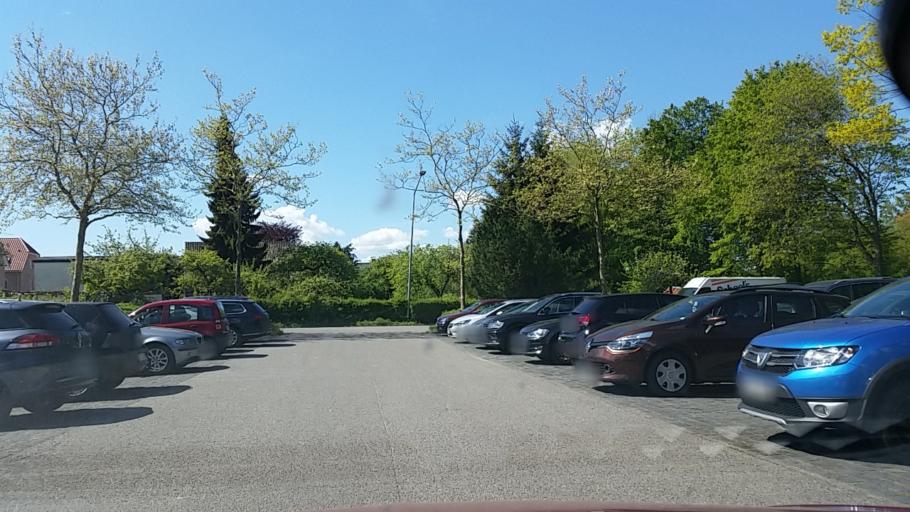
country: DE
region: Schleswig-Holstein
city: Neustadt in Holstein
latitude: 54.1067
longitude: 10.8061
